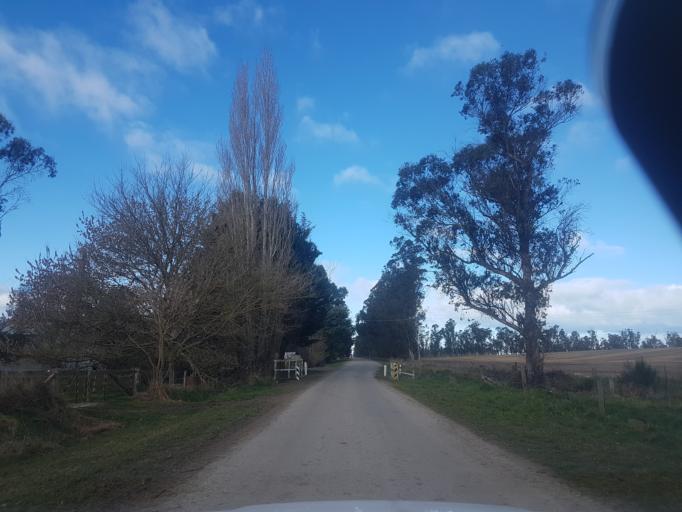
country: NZ
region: Canterbury
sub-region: Timaru District
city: Pleasant Point
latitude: -44.2073
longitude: 171.2073
